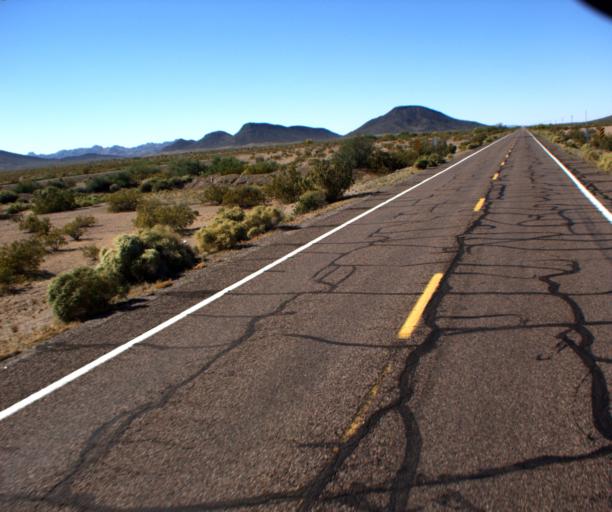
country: US
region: Arizona
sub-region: Maricopa County
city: Gila Bend
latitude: 32.7904
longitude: -112.8050
